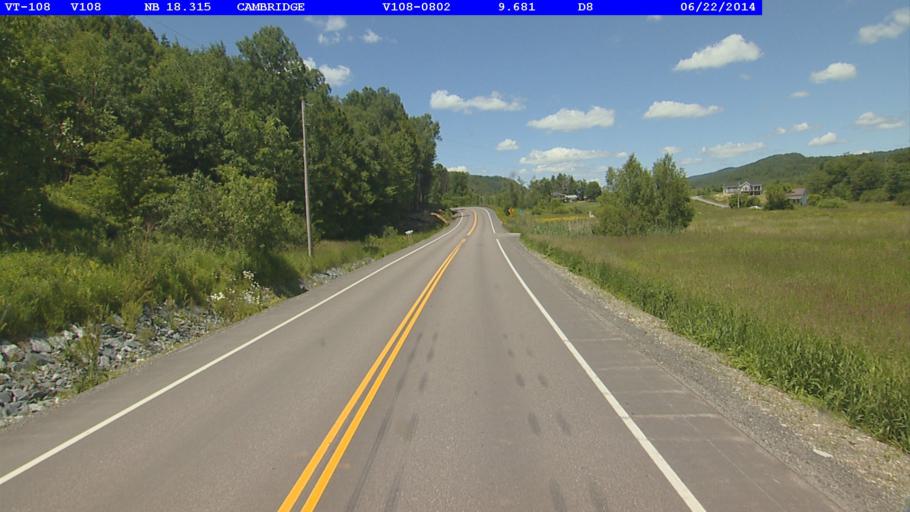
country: US
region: Vermont
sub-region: Lamoille County
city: Johnson
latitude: 44.6557
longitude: -72.8284
